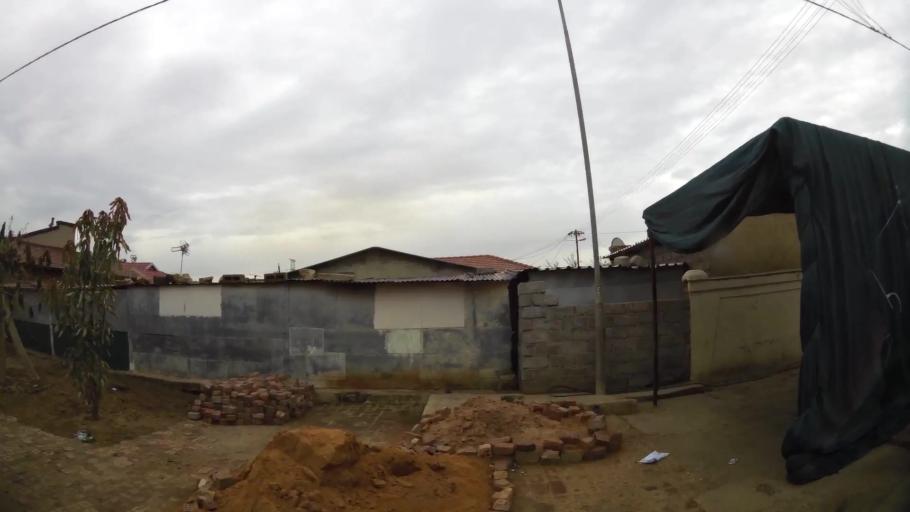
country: ZA
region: Gauteng
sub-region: City of Tshwane Metropolitan Municipality
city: Cullinan
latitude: -25.7193
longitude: 28.3620
